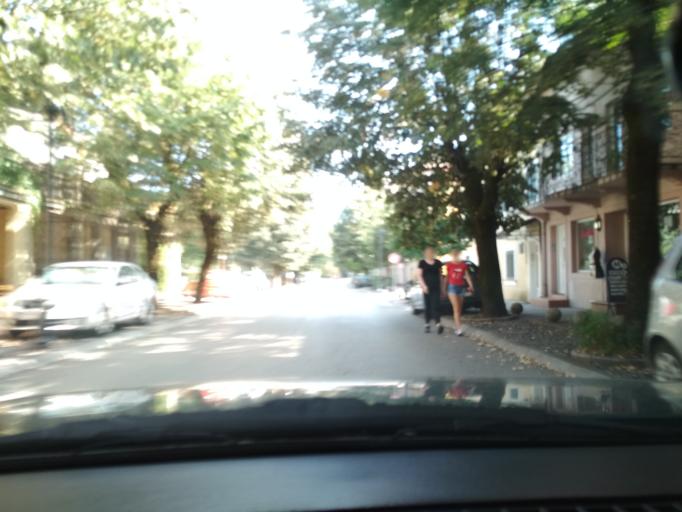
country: ME
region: Cetinje
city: Cetinje
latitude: 42.3888
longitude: 18.9259
